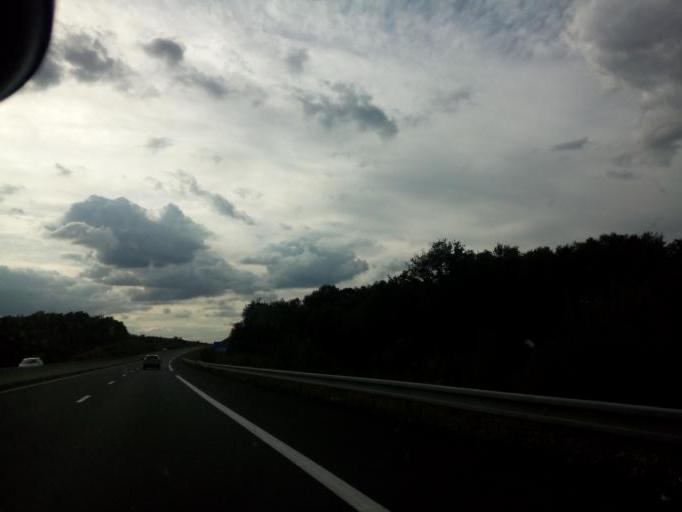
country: FR
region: Centre
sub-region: Departement du Loir-et-Cher
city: Faverolles-sur-Cher
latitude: 47.2956
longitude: 1.2420
